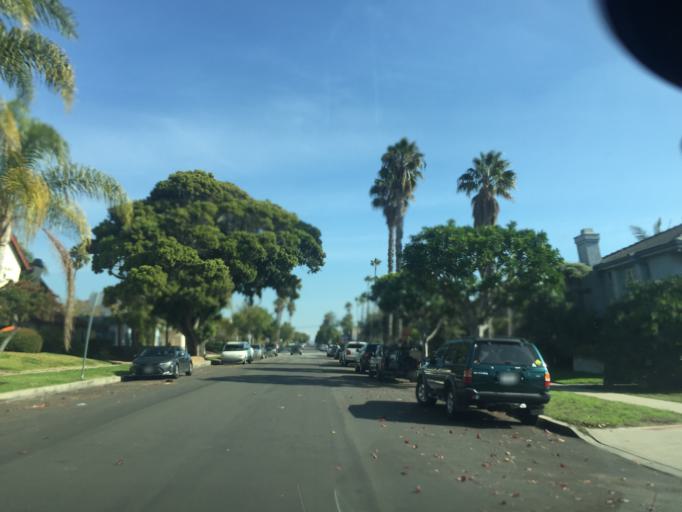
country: US
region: California
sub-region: San Diego County
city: La Jolla
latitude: 32.7954
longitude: -117.2466
